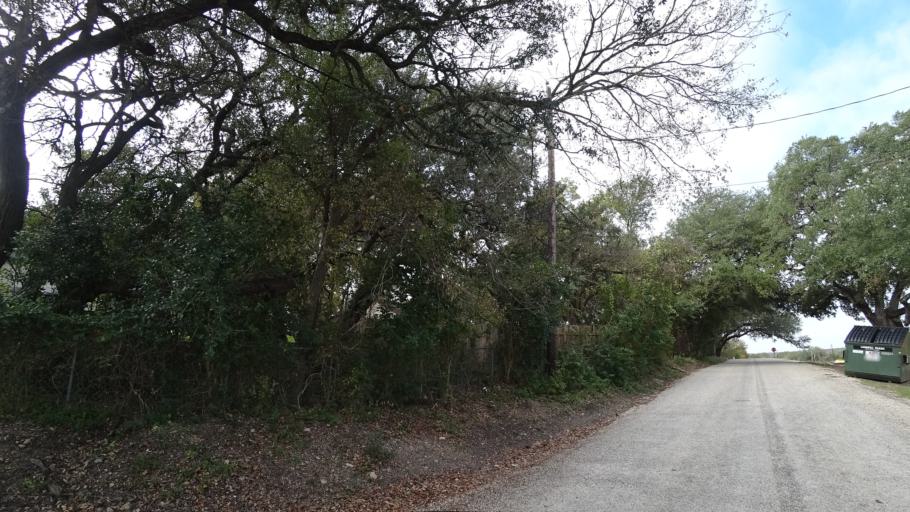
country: US
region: Texas
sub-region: Travis County
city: Manchaca
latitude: 30.1248
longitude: -97.8622
